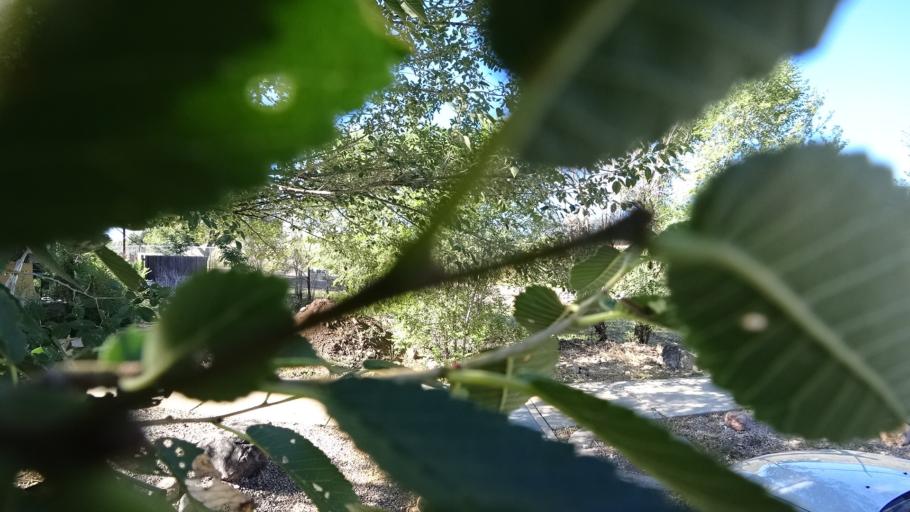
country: US
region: Colorado
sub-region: El Paso County
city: Colorado Springs
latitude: 38.8194
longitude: -104.8306
